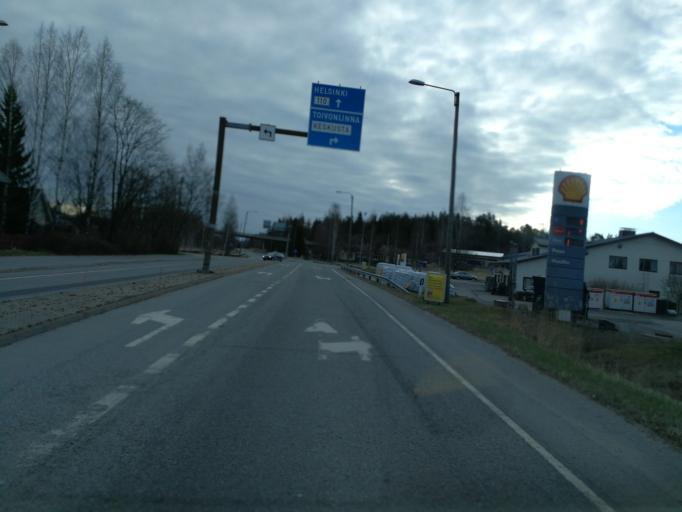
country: FI
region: Varsinais-Suomi
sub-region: Turku
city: Piikkioe
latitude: 60.4230
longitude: 22.5231
